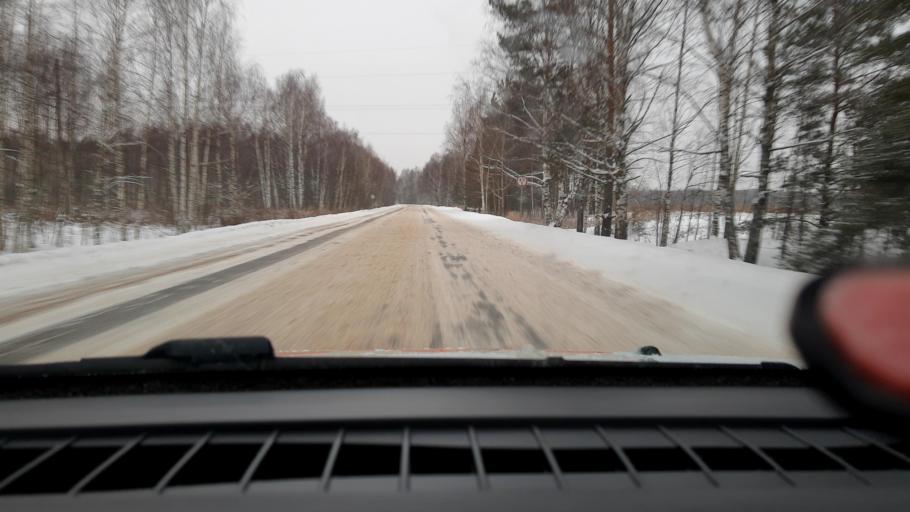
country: RU
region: Nizjnij Novgorod
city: Pamyat' Parizhskoy Kommuny
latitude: 56.2626
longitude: 44.4443
